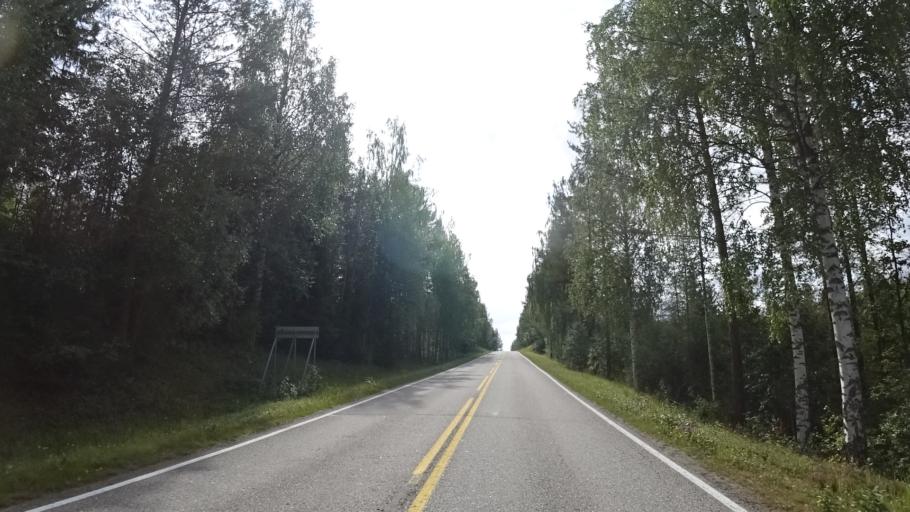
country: FI
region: North Karelia
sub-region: Joensuu
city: Ilomantsi
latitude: 62.7566
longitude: 31.0067
